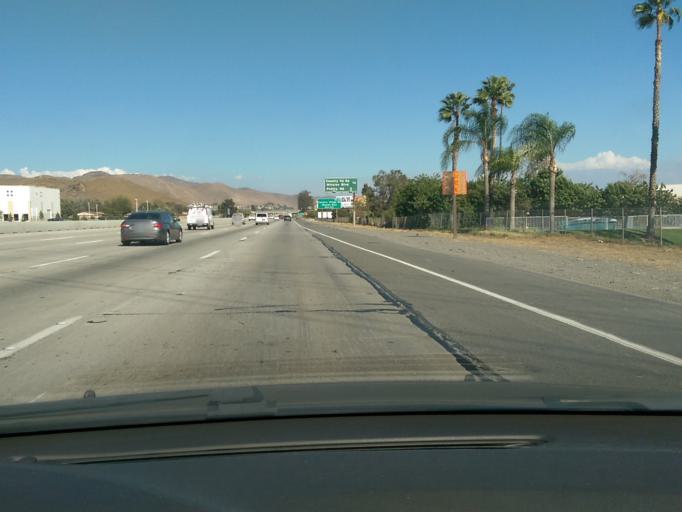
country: US
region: California
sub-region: Riverside County
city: Mira Loma
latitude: 34.0180
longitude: -117.5212
